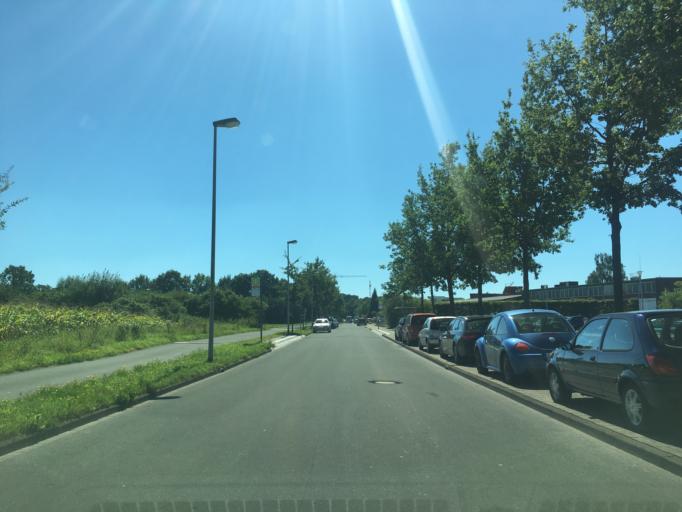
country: DE
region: North Rhine-Westphalia
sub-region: Regierungsbezirk Munster
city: Muenster
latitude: 51.9879
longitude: 7.6215
